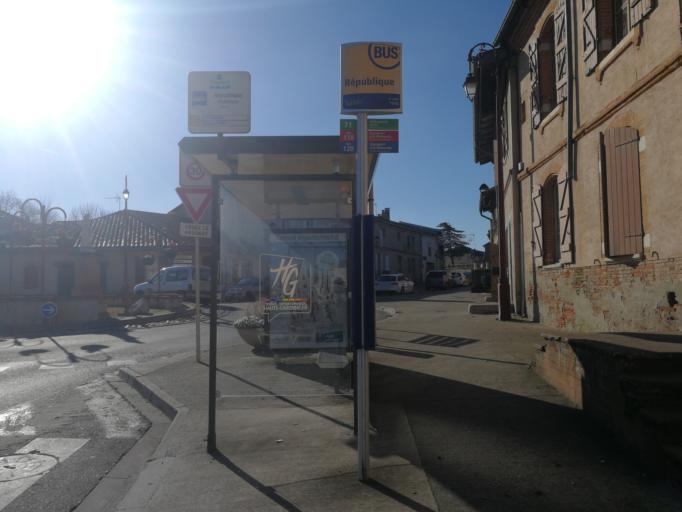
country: FR
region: Midi-Pyrenees
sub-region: Departement de la Haute-Garonne
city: Aussonne
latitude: 43.6836
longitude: 1.3203
